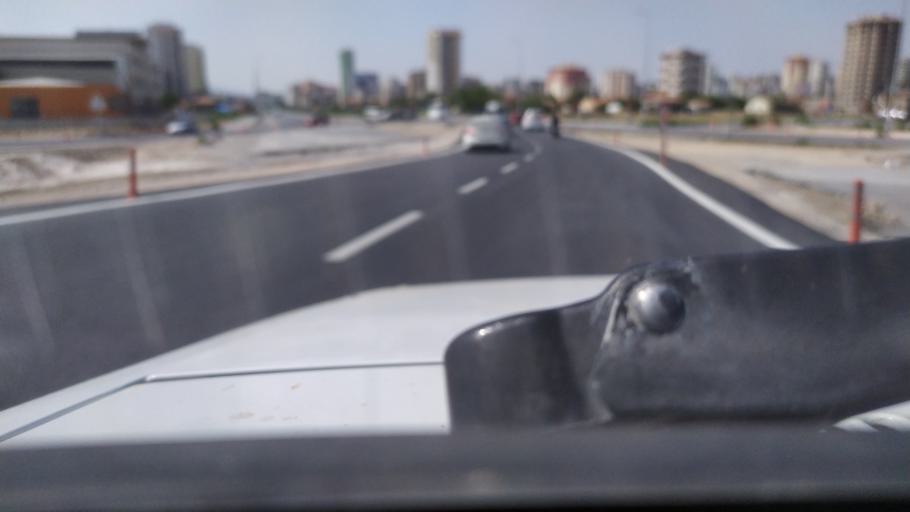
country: TR
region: Kayseri
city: Talas
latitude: 38.7199
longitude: 35.5479
